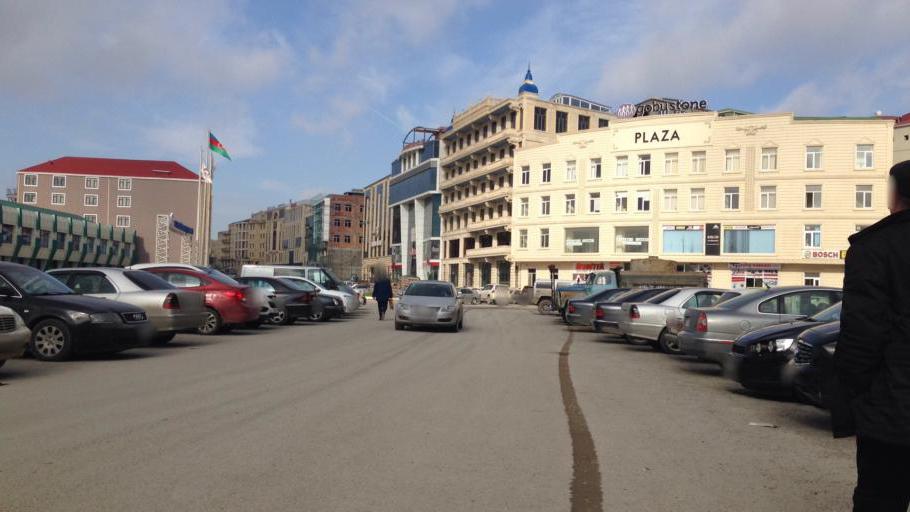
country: AZ
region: Baki
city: Baku
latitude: 40.4126
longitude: 49.8603
